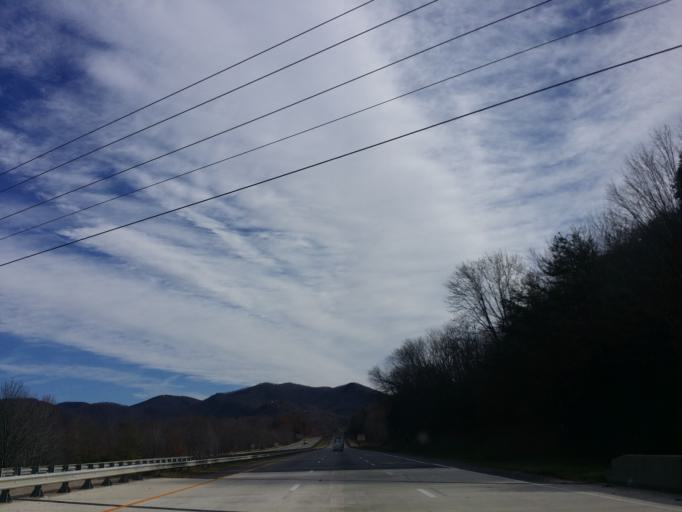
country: US
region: North Carolina
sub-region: Buncombe County
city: Black Mountain
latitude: 35.6121
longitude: -82.3188
